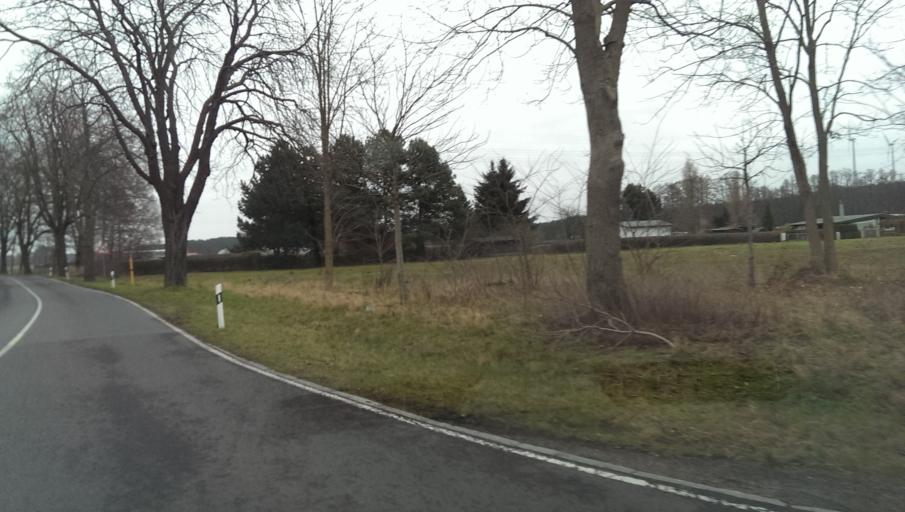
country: DE
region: Brandenburg
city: Zossen
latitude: 52.2238
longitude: 13.4888
